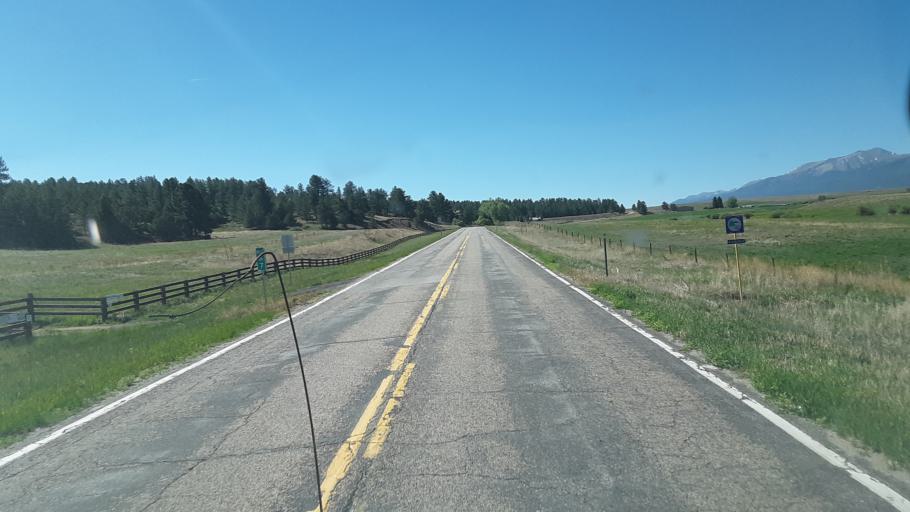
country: US
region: Colorado
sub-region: Custer County
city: Westcliffe
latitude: 38.2262
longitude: -105.5539
